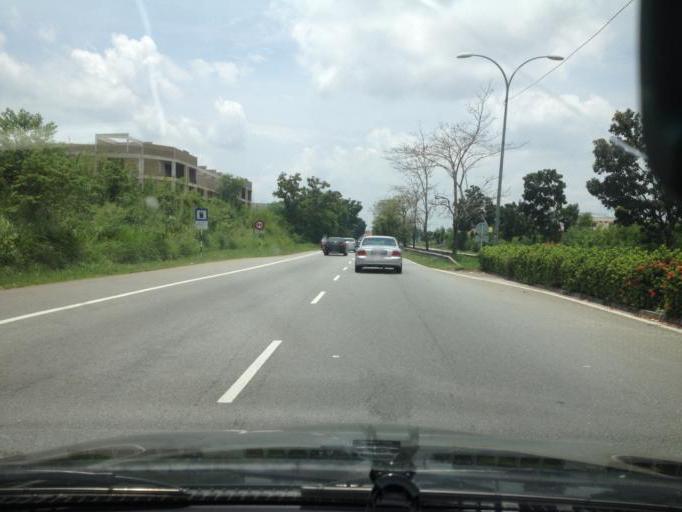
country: MY
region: Kedah
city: Sungai Petani
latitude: 5.6354
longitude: 100.5394
